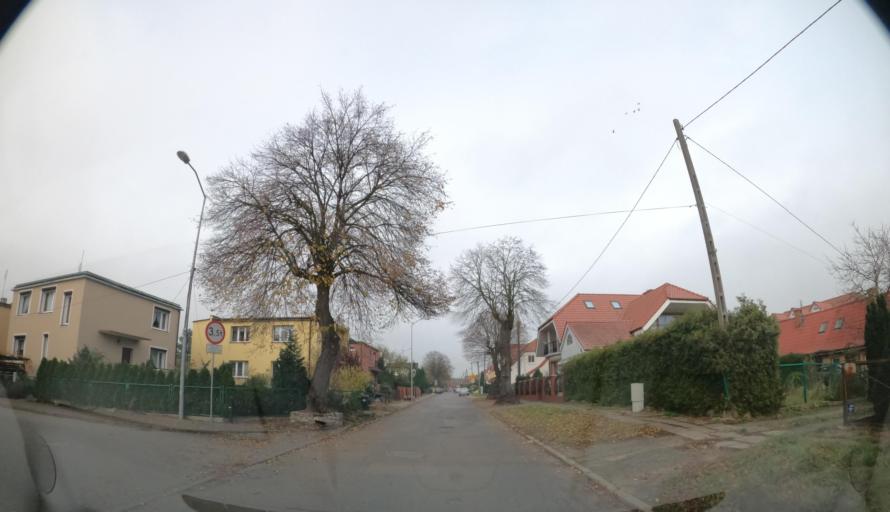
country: PL
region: West Pomeranian Voivodeship
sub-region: Powiat goleniowski
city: Goleniow
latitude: 53.5706
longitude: 14.8367
